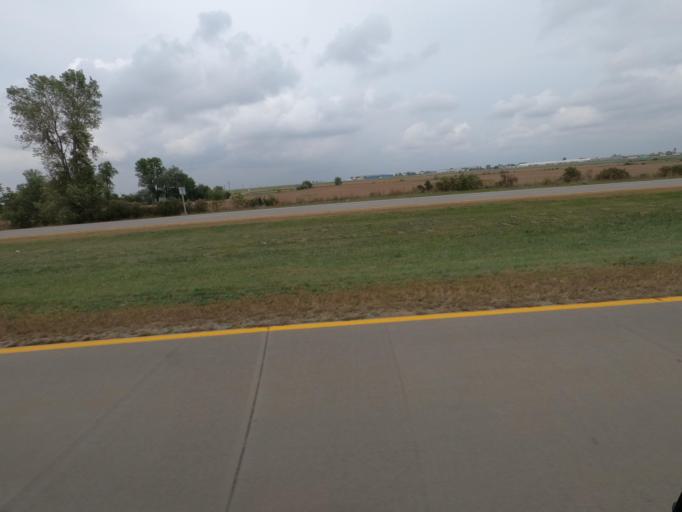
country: US
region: Iowa
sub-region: Wapello County
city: Ottumwa
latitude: 41.0948
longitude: -92.4476
